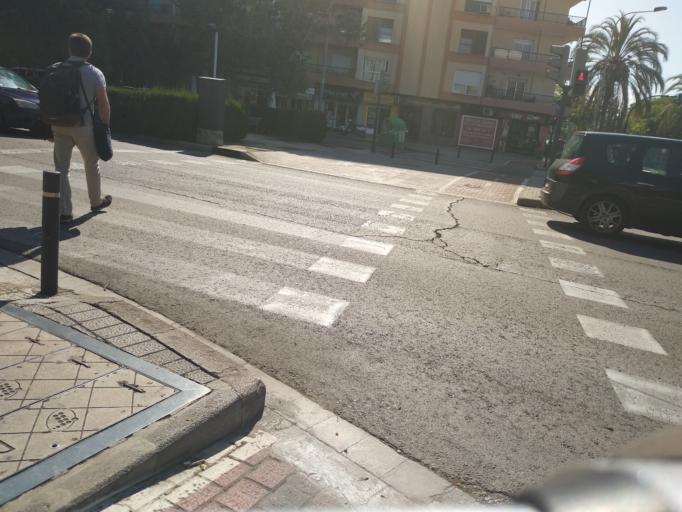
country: ES
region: Valencia
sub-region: Provincia de Valencia
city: Alboraya
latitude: 39.4780
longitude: -0.3459
